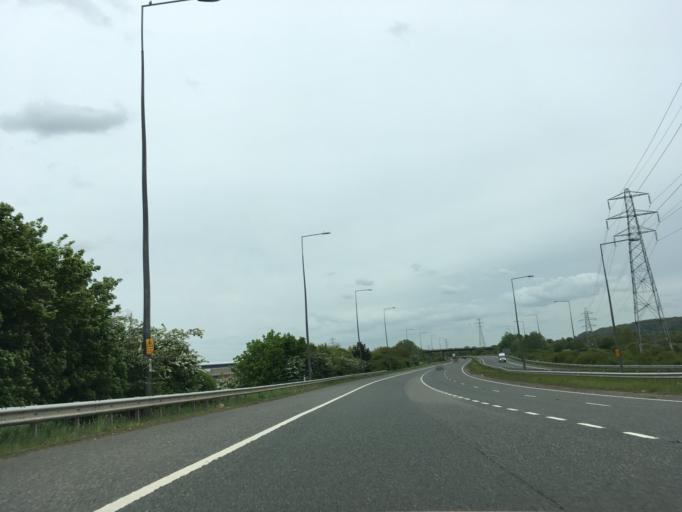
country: GB
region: England
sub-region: North Somerset
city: Easton-in-Gordano
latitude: 51.5086
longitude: -2.6675
